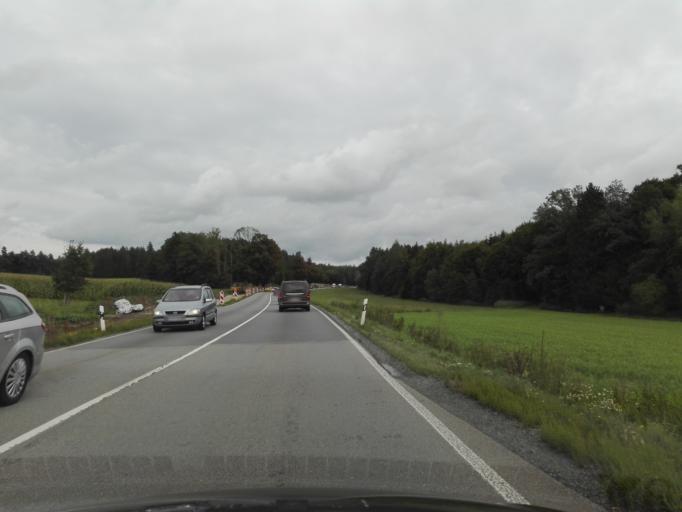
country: DE
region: Bavaria
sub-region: Upper Bavaria
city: Hohenlinden
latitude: 48.1397
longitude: 12.0351
